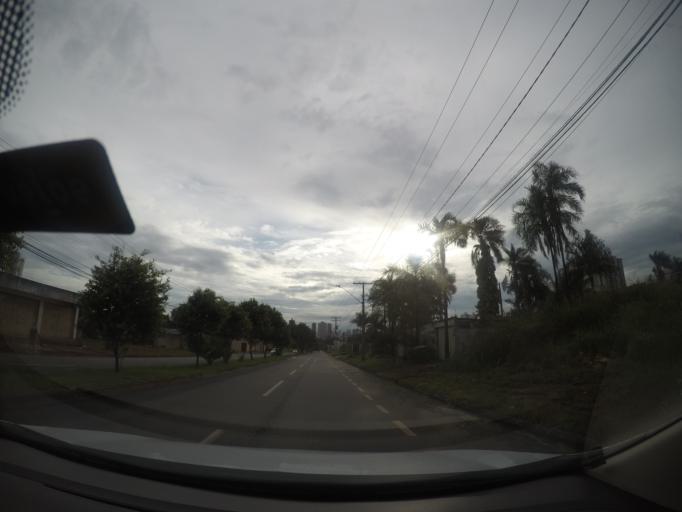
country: BR
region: Goias
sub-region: Goiania
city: Goiania
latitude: -16.7409
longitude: -49.2963
